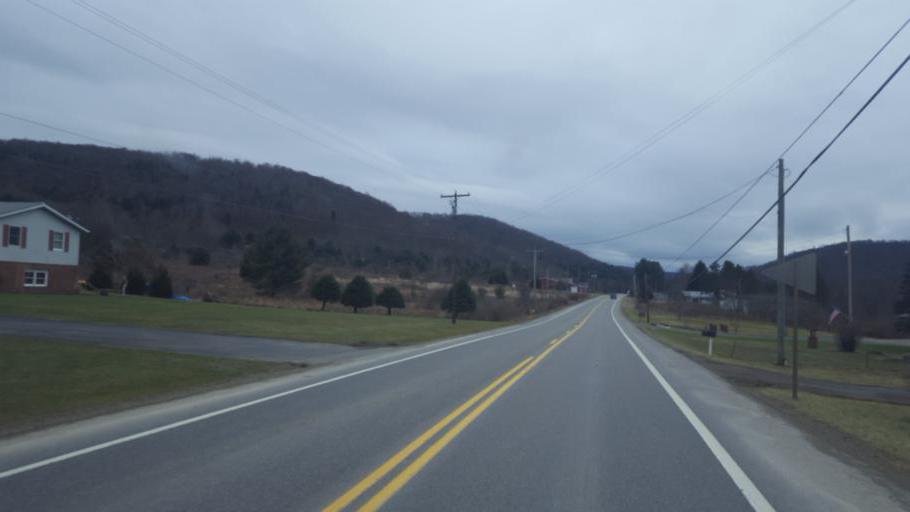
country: US
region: Pennsylvania
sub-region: Potter County
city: Coudersport
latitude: 41.7641
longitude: -78.1172
